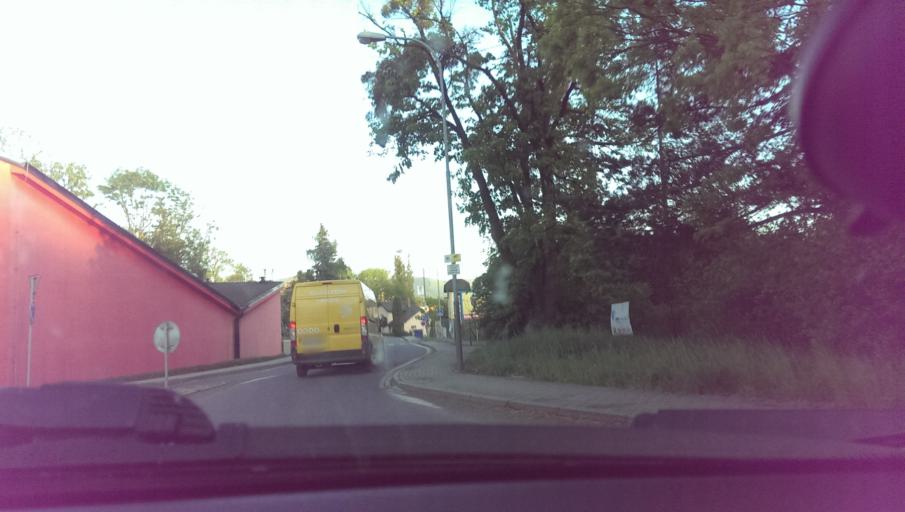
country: CZ
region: Moravskoslezsky
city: Frenstat pod Radhostem
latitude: 49.5511
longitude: 18.1996
